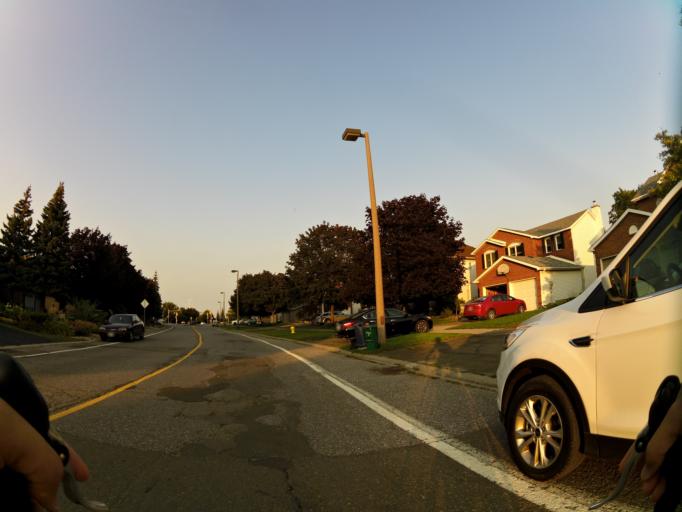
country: CA
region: Ontario
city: Bells Corners
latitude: 45.3501
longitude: -75.9291
